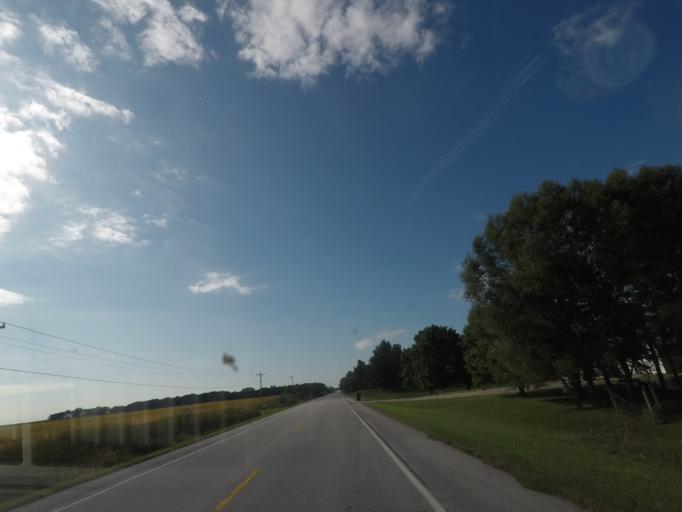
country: US
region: Iowa
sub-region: Story County
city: Nevada
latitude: 41.9970
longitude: -93.4446
